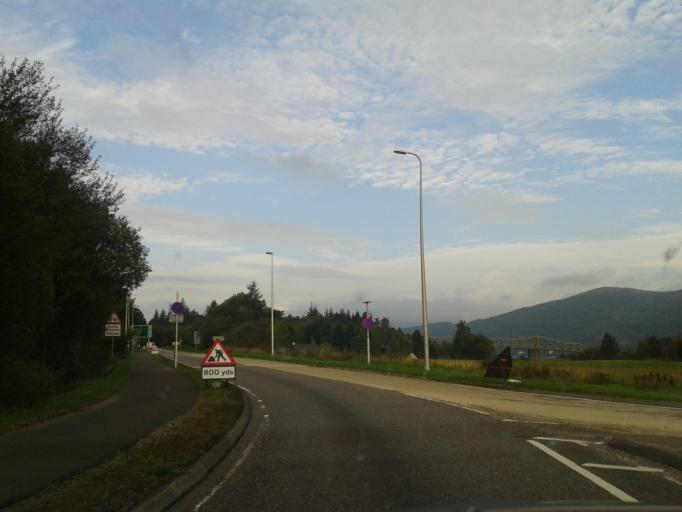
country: GB
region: Scotland
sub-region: Highland
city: Fort William
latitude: 56.6846
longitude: -5.1745
